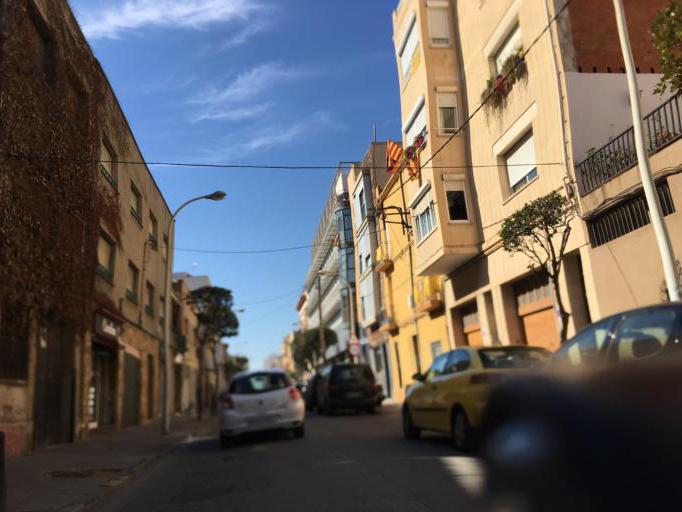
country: ES
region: Catalonia
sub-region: Provincia de Barcelona
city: Badalona
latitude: 41.4453
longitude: 2.2469
